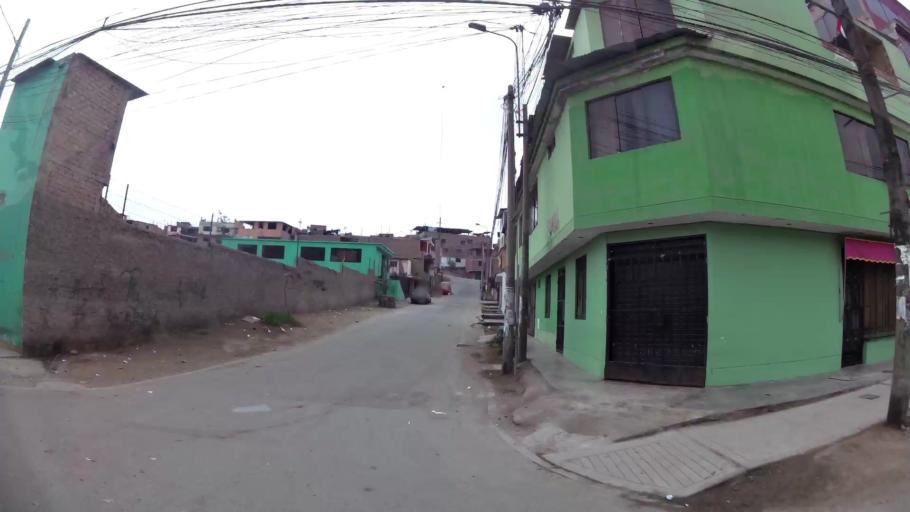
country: PE
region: Lima
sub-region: Lima
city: Surco
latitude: -12.1394
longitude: -76.9597
